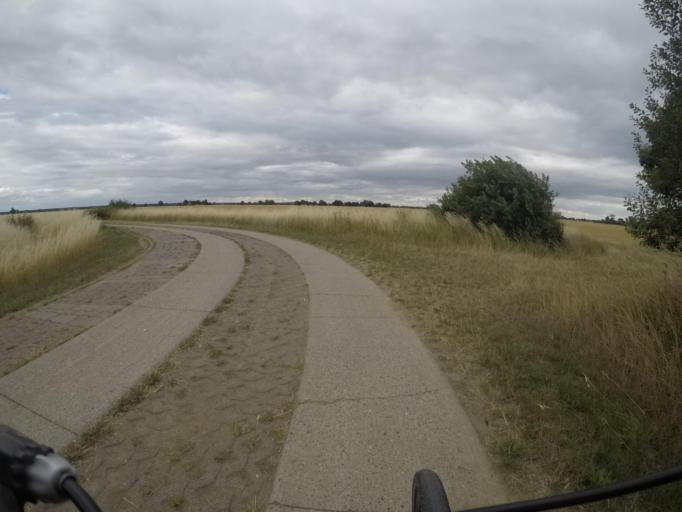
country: DE
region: Lower Saxony
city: Neu Darchau
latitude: 53.2430
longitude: 10.9116
